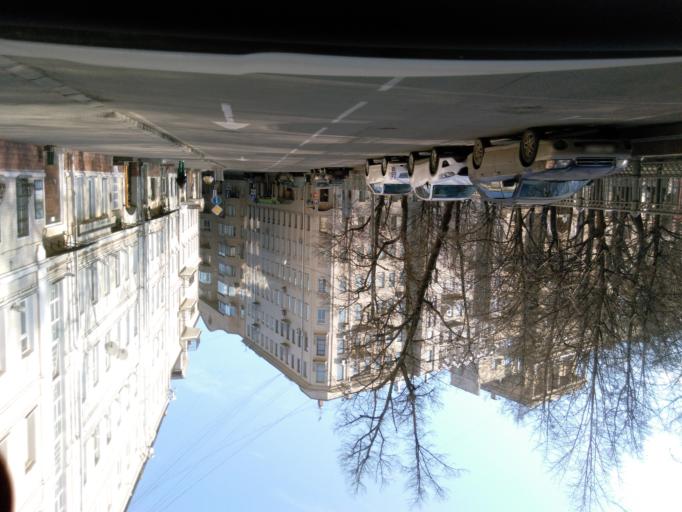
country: RU
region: Moscow
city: Moscow
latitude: 55.7644
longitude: 37.5909
